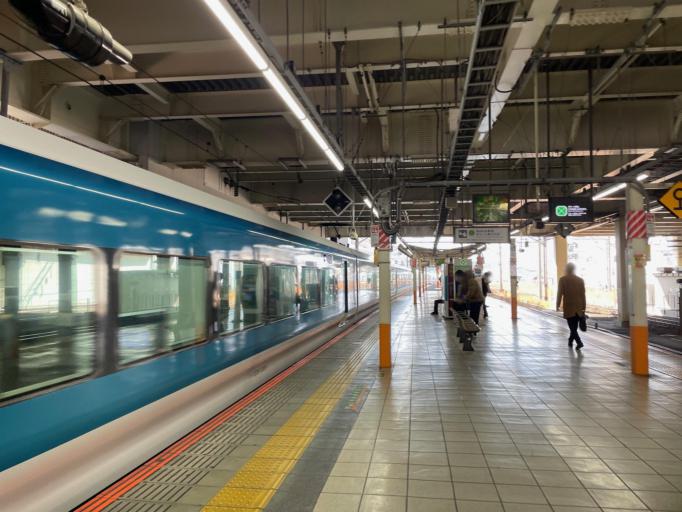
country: JP
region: Kanagawa
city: Chigasaki
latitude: 35.3302
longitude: 139.4065
